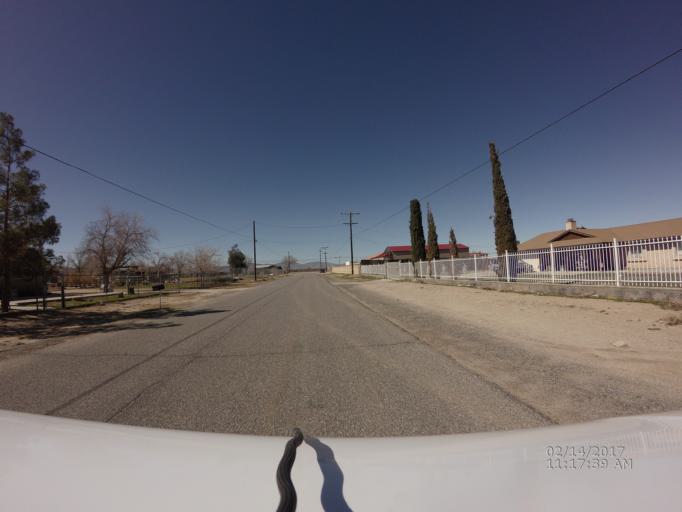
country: US
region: California
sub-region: Los Angeles County
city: Littlerock
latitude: 34.5632
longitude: -117.9681
